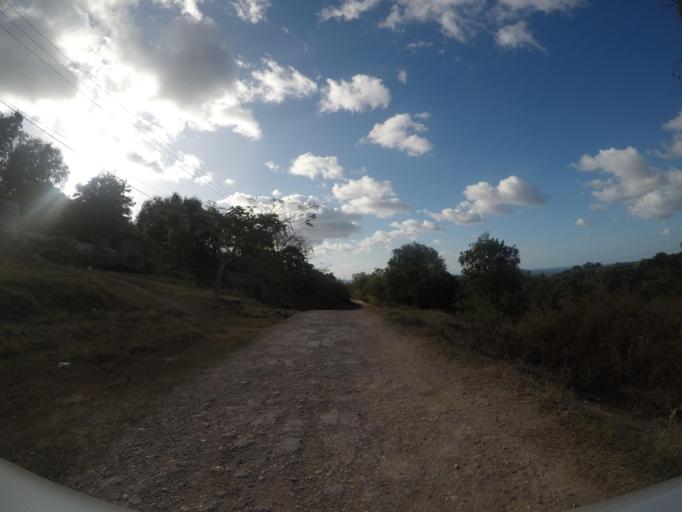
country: TL
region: Lautem
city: Lospalos
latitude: -8.4310
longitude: 126.8477
